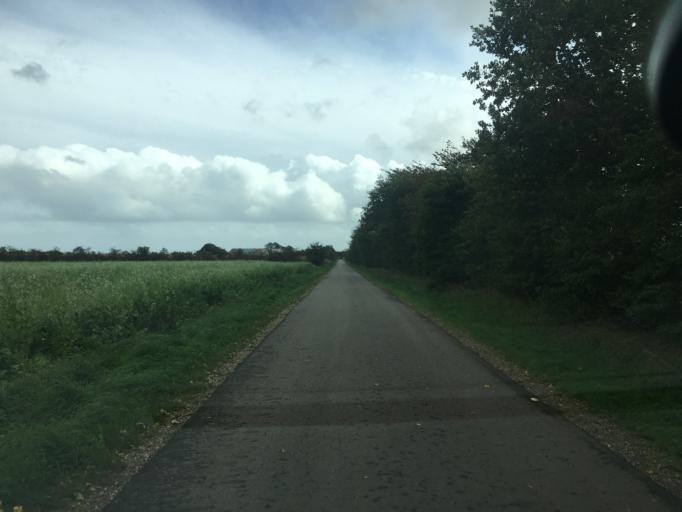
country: DK
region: South Denmark
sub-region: Tonder Kommune
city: Sherrebek
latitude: 55.0793
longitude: 8.8128
